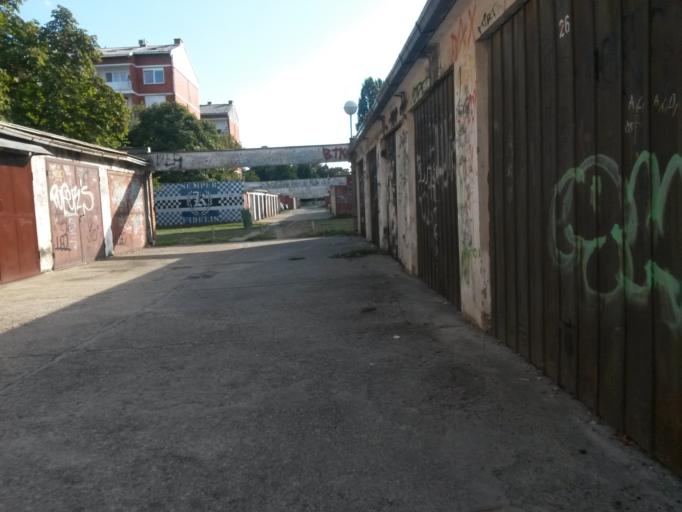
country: HR
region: Osjecko-Baranjska
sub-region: Grad Osijek
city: Osijek
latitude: 45.5462
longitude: 18.7250
